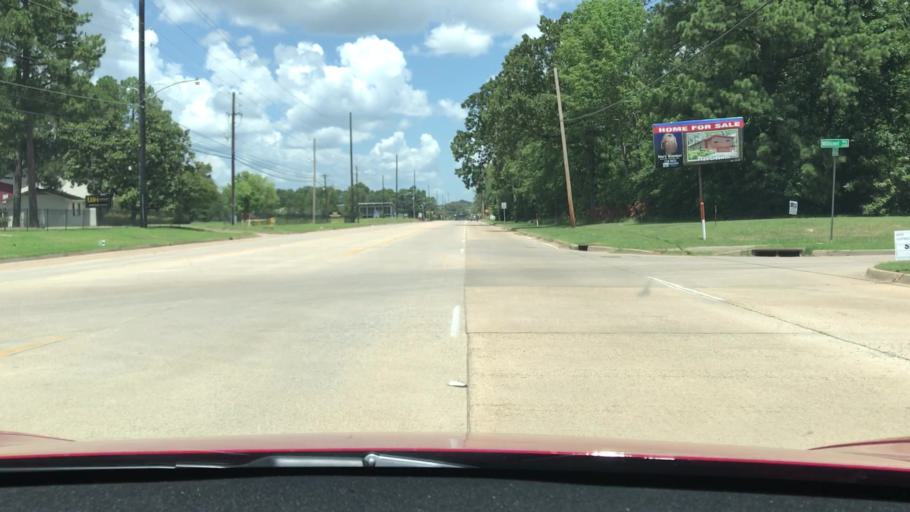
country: US
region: Louisiana
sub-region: Bossier Parish
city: Bossier City
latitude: 32.4252
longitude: -93.7397
